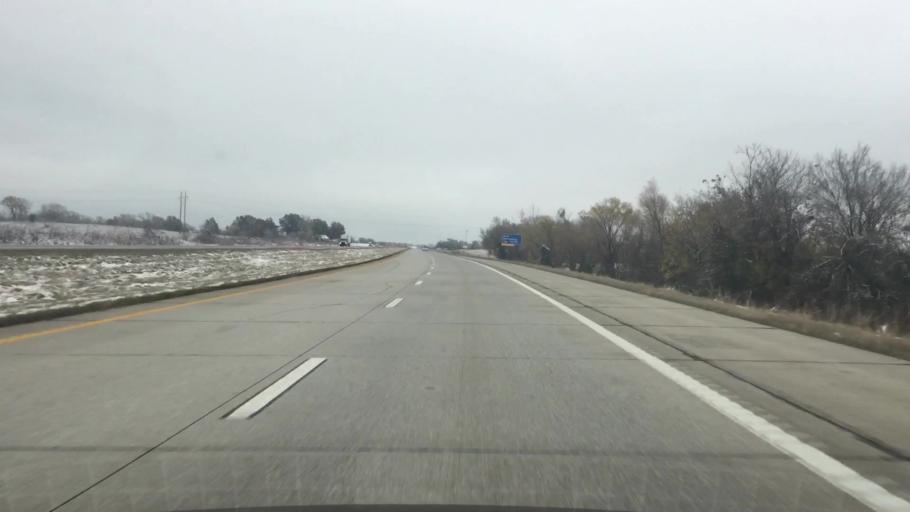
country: US
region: Missouri
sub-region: Saint Clair County
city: Osceola
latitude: 38.1880
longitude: -93.7380
